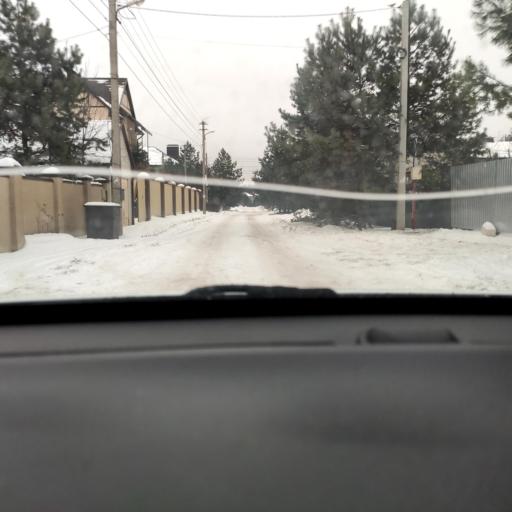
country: RU
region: Voronezj
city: Somovo
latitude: 51.7114
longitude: 39.3169
